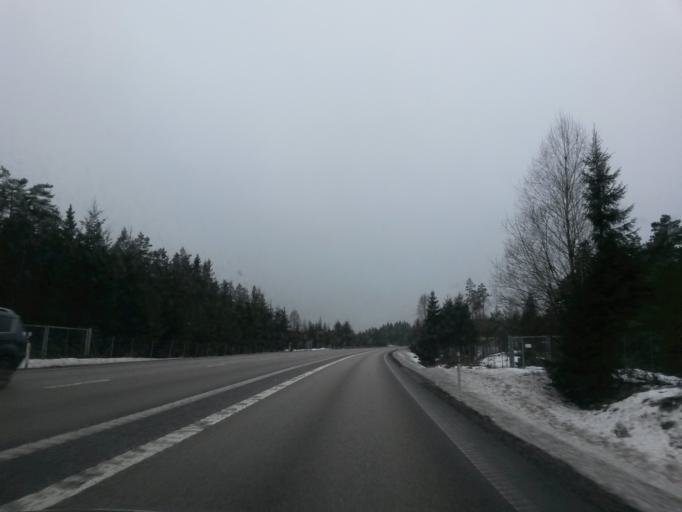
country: SE
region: Vaestra Goetaland
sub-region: Marks Kommun
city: Fritsla
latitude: 57.5489
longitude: 12.8216
